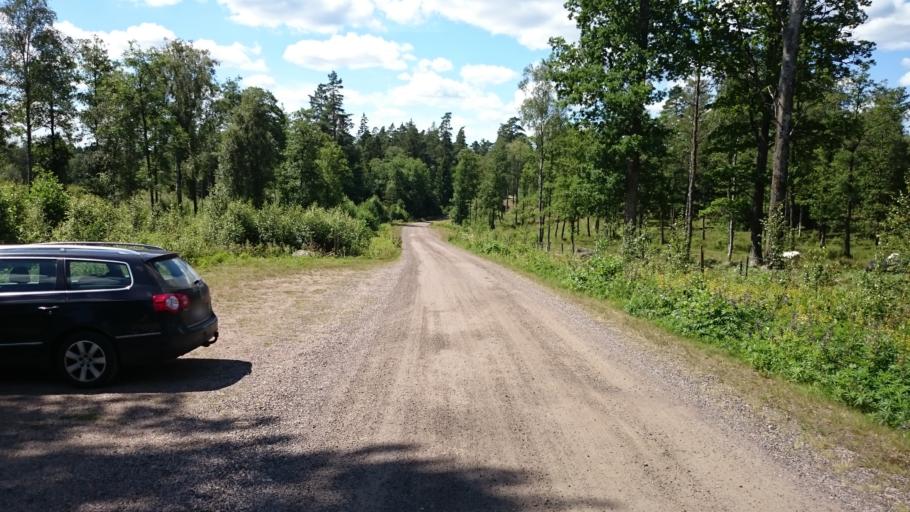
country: SE
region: Halland
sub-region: Hylte Kommun
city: Hyltebruk
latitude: 56.9736
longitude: 13.1675
